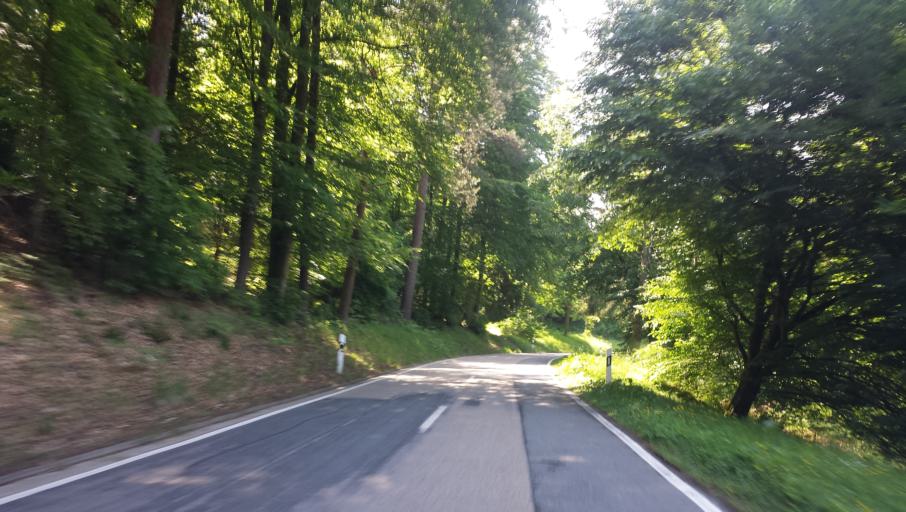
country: DE
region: Hesse
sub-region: Regierungsbezirk Darmstadt
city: Rothenberg
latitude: 49.5524
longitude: 8.8996
